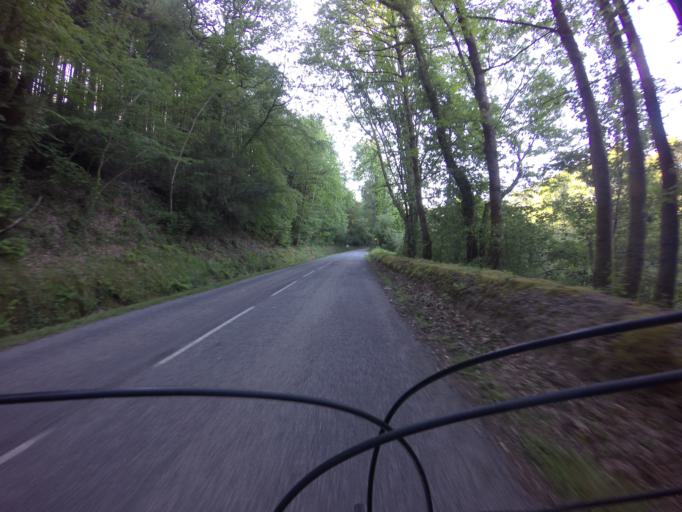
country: FR
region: Brittany
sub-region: Departement du Finistere
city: Quimper
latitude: 48.0253
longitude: -4.1447
